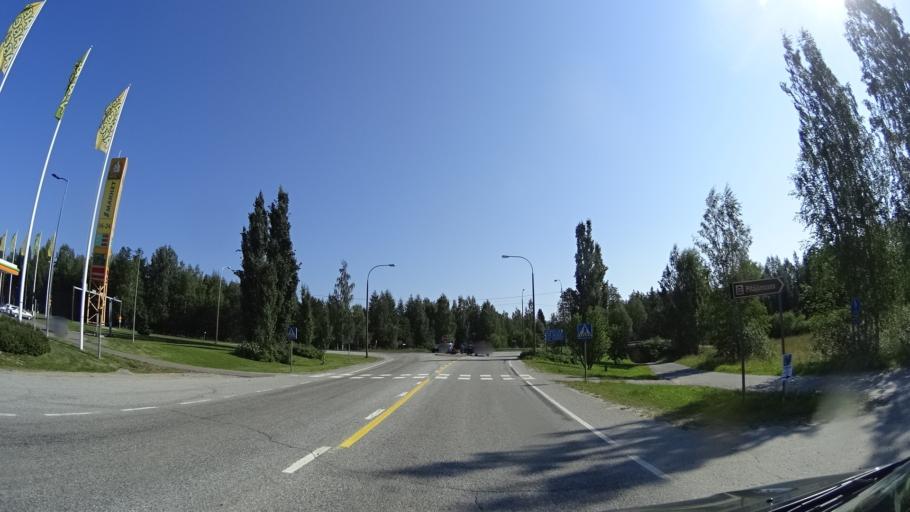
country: FI
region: North Karelia
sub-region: Joensuu
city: Juuka
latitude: 63.2466
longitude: 29.2659
